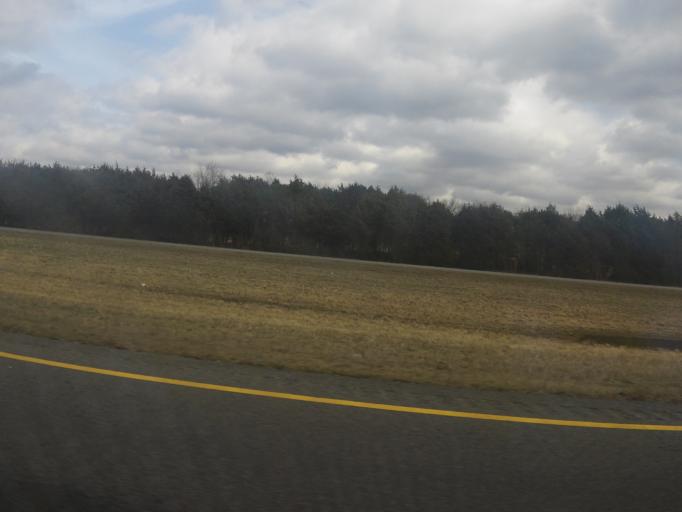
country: US
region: Tennessee
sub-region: Rutherford County
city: Plainview
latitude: 35.6850
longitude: -86.2920
